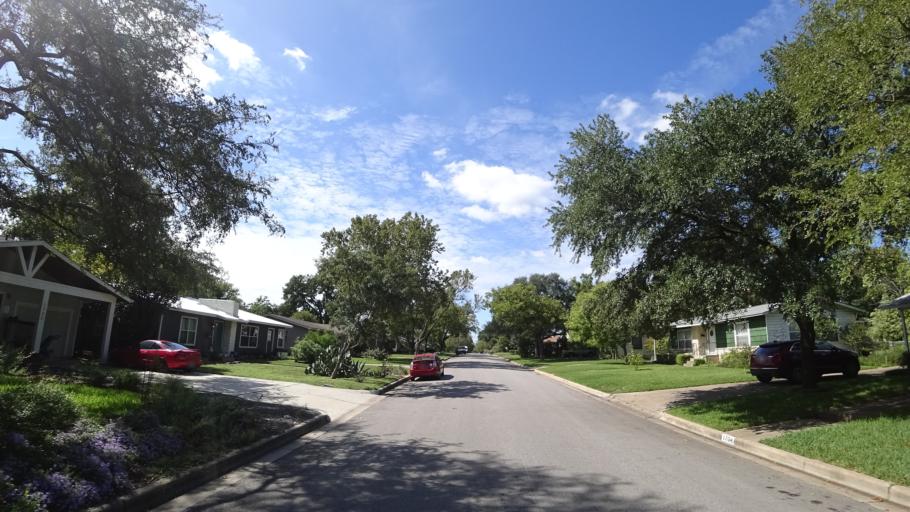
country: US
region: Texas
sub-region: Travis County
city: Austin
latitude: 30.3469
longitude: -97.7268
